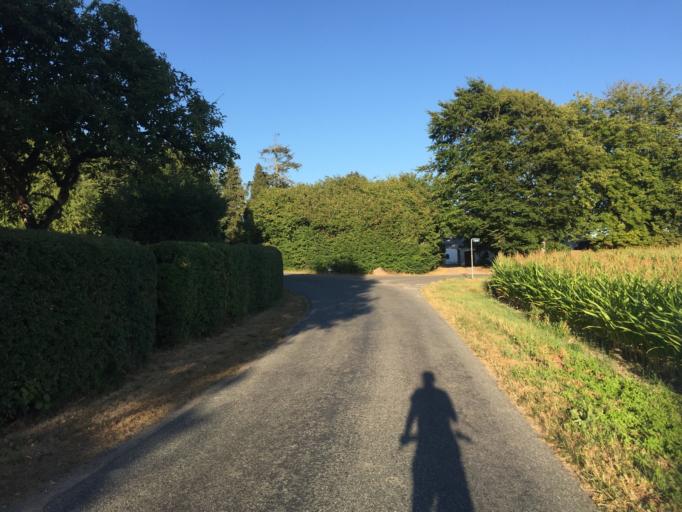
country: DK
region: South Denmark
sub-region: Odense Kommune
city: Bellinge
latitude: 55.3679
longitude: 10.2811
